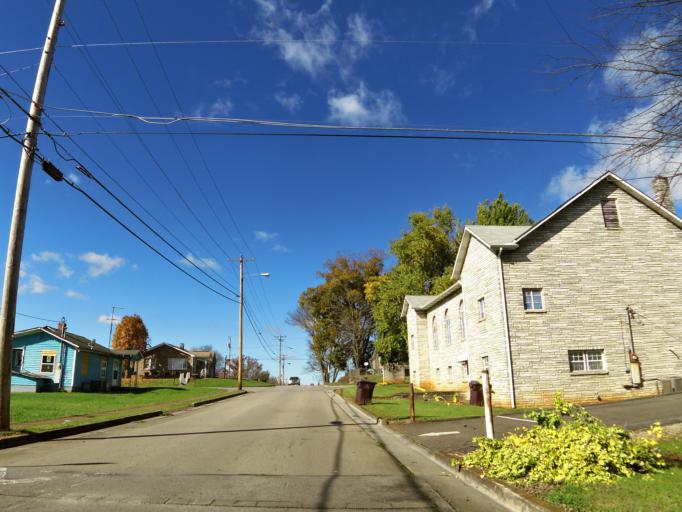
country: US
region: Tennessee
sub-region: Blount County
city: Alcoa
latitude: 35.7768
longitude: -83.9823
